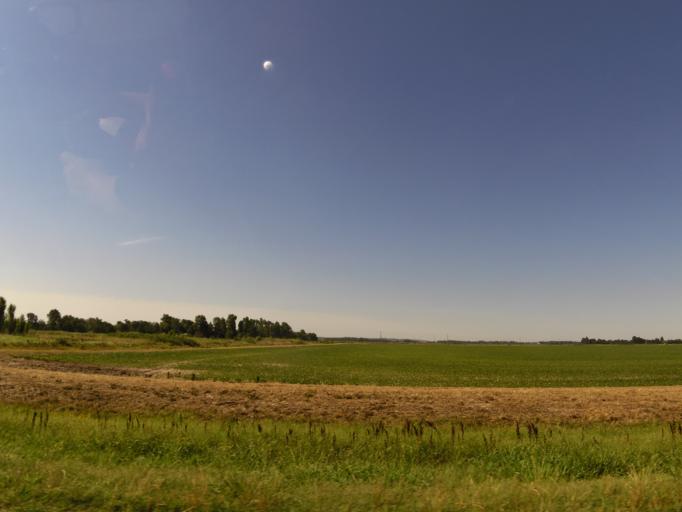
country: US
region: Arkansas
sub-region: Clay County
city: Corning
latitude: 36.4346
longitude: -90.4013
